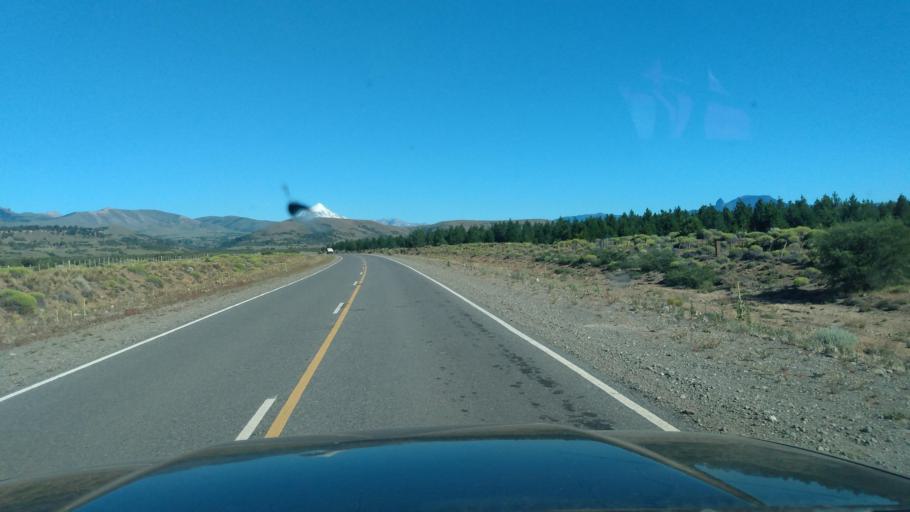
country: AR
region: Neuquen
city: Junin de los Andes
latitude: -39.8775
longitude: -71.1675
